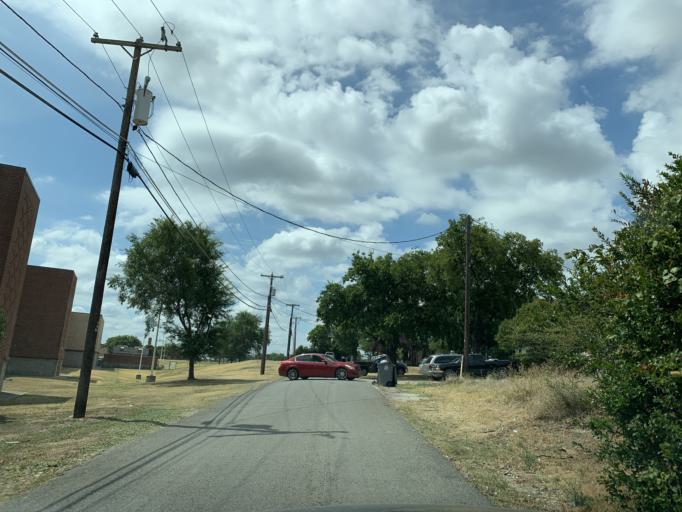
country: US
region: Texas
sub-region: Dallas County
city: Cockrell Hill
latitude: 32.7637
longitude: -96.8665
